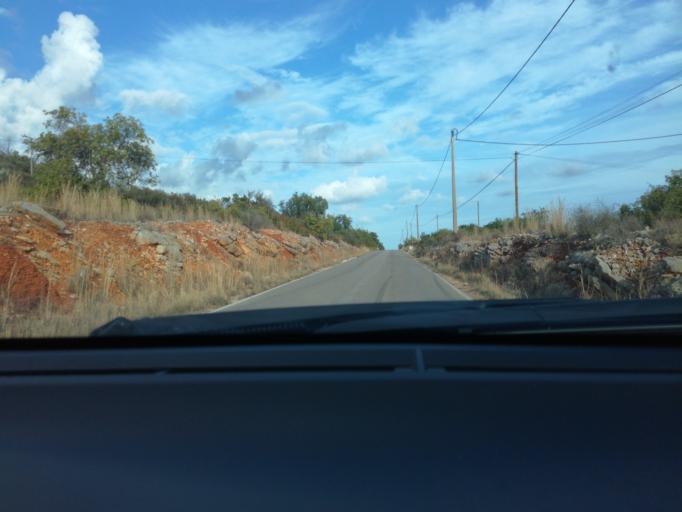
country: PT
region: Faro
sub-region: Olhao
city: Laranjeiro
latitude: 37.0789
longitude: -7.8163
